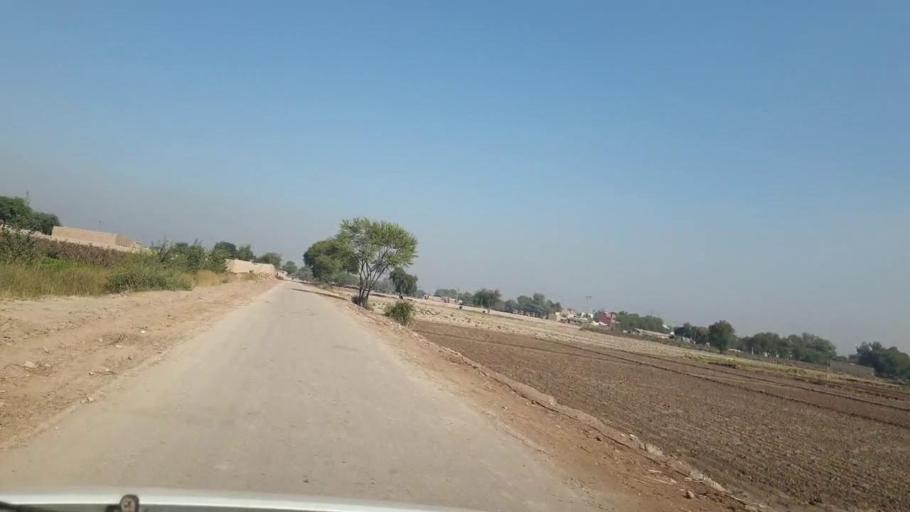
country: PK
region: Sindh
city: Bhan
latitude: 26.6081
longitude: 67.7341
